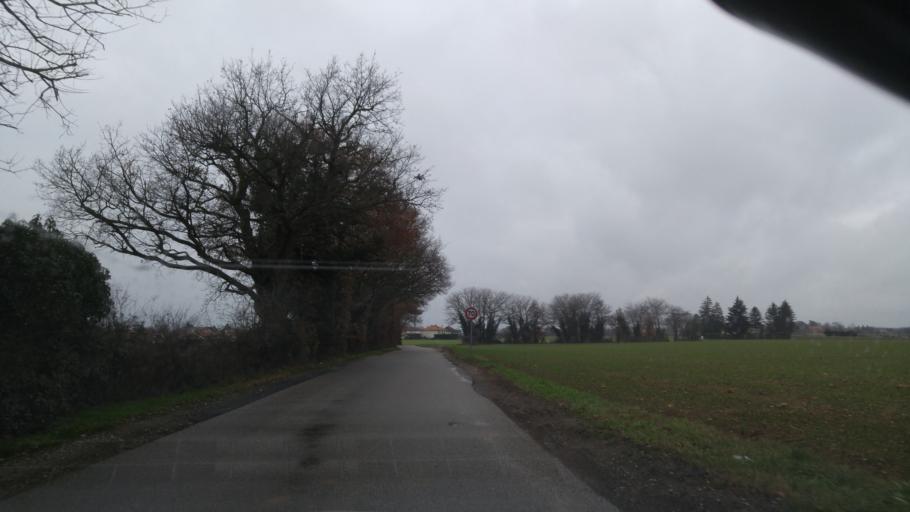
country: FR
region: Rhone-Alpes
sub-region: Departement du Rhone
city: Saint-Laurent-de-Mure
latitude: 45.6979
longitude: 5.0400
